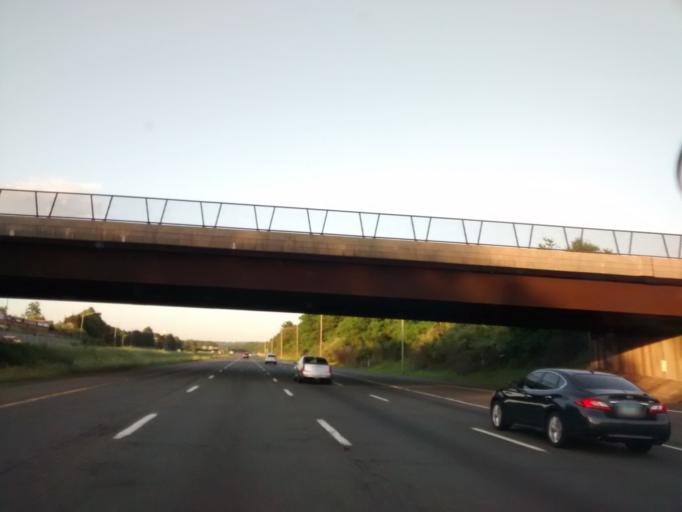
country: US
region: Connecticut
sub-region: Tolland County
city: Rockville
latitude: 41.8256
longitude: -72.4892
